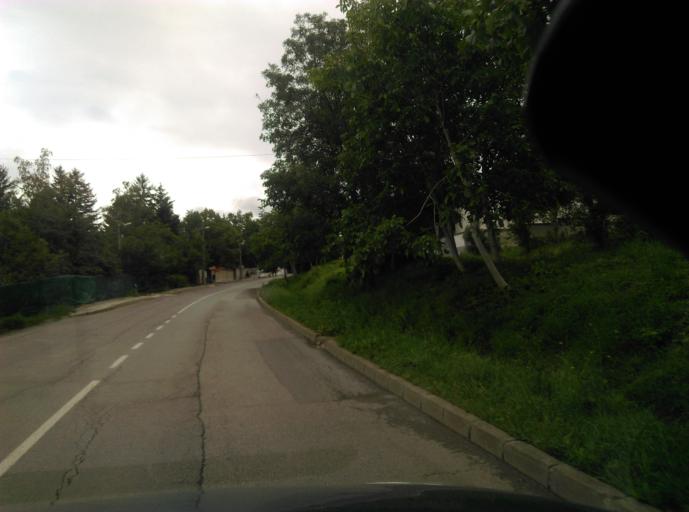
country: BG
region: Sofia-Capital
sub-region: Stolichna Obshtina
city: Sofia
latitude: 42.6194
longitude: 23.3327
